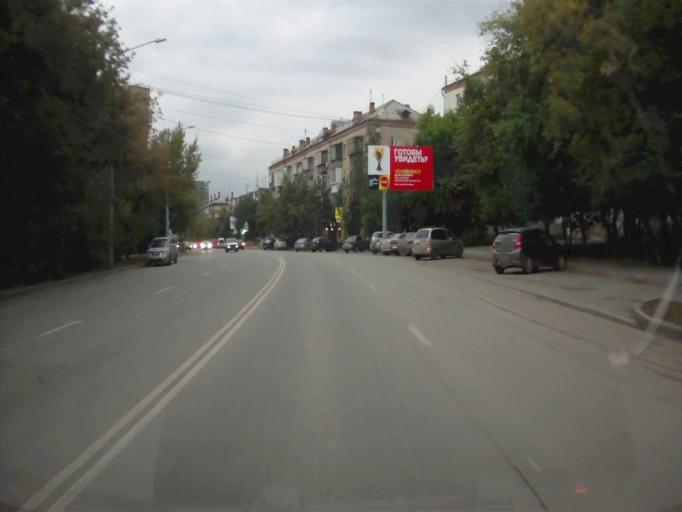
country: RU
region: Chelyabinsk
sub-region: Gorod Chelyabinsk
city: Chelyabinsk
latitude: 55.1540
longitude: 61.3986
